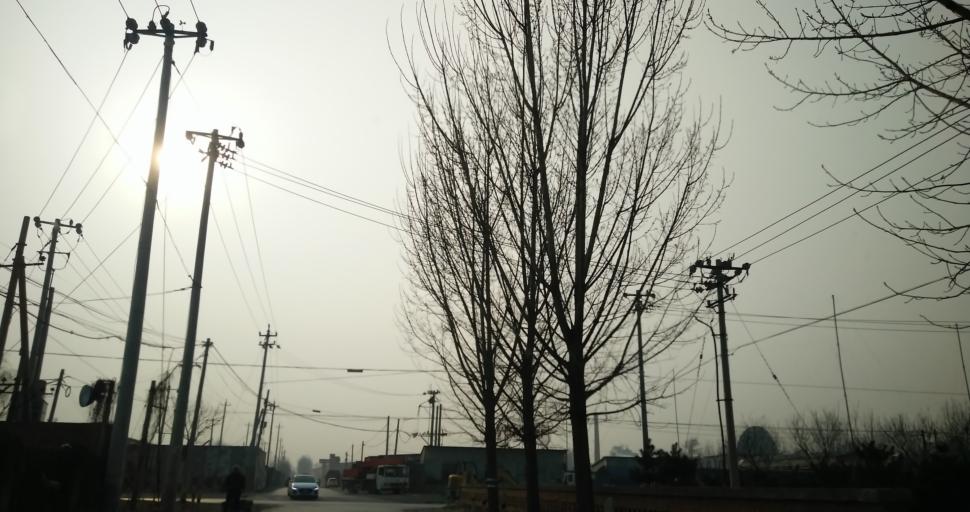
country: CN
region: Beijing
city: Xingfeng
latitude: 39.7120
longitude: 116.3613
